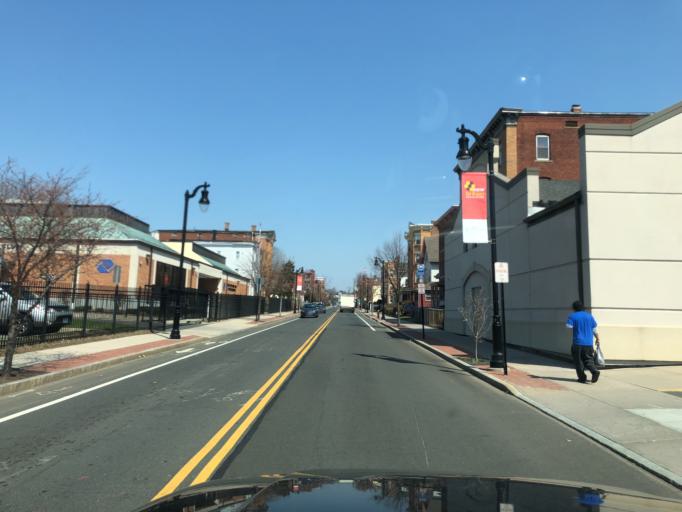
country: US
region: Connecticut
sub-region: Hartford County
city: New Britain
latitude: 41.6708
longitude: -72.7841
